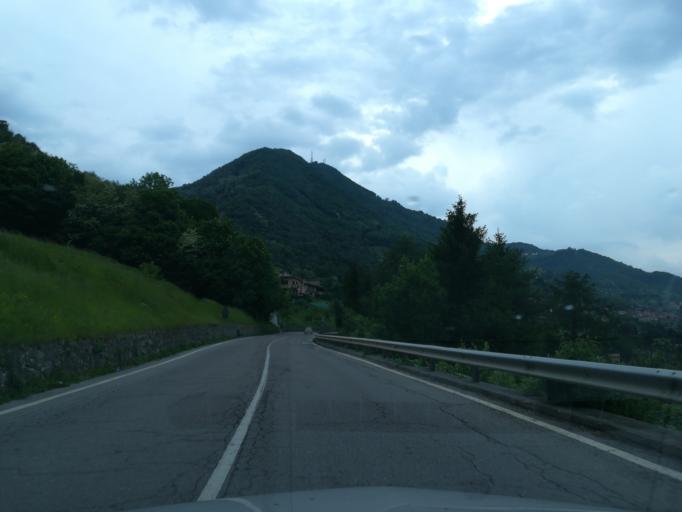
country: IT
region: Lombardy
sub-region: Provincia di Bergamo
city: Strozza
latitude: 45.7640
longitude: 9.5889
